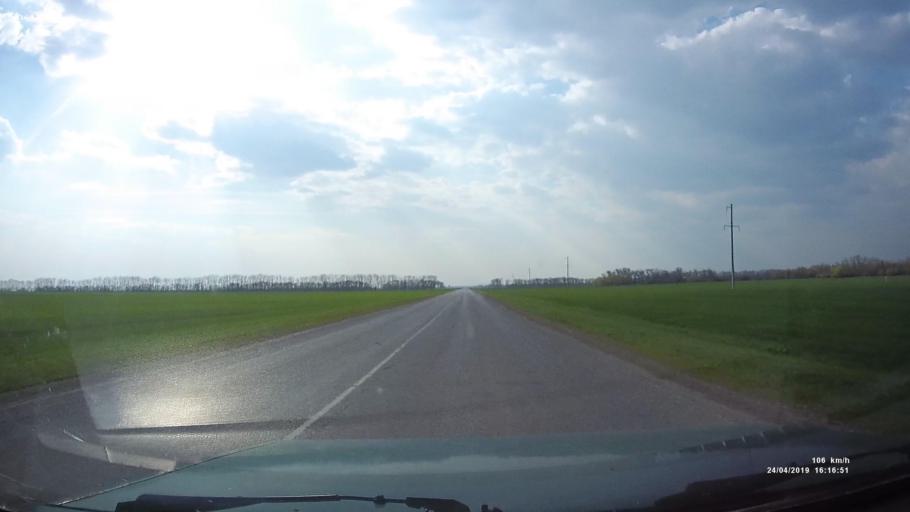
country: RU
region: Rostov
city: Sovetskoye
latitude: 46.7654
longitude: 42.1509
